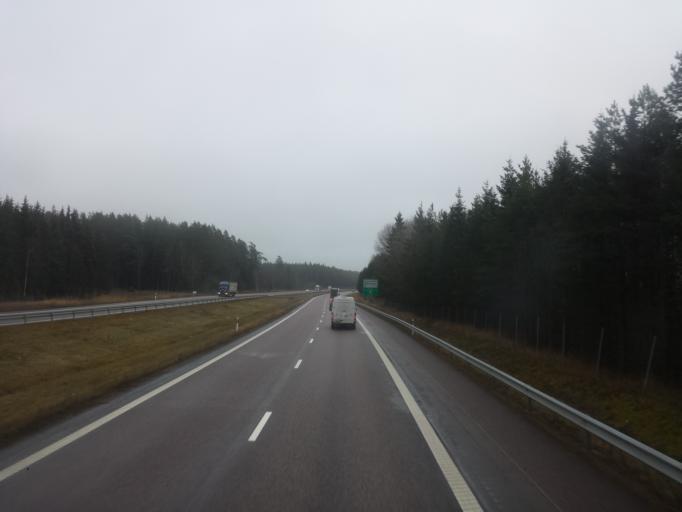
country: SE
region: Soedermanland
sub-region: Nykopings Kommun
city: Svalsta
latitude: 58.7570
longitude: 16.8310
